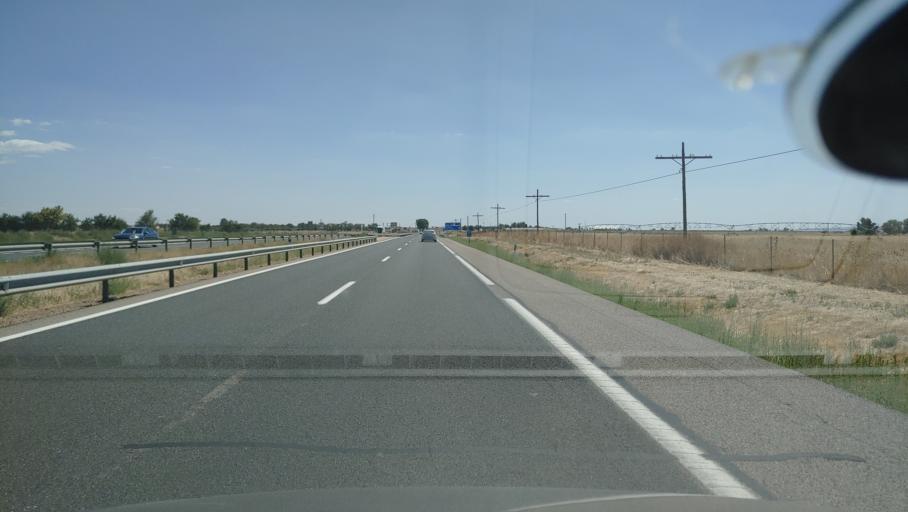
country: ES
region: Castille-La Mancha
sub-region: Provincia de Ciudad Real
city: Villarta de San Juan
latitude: 39.1326
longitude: -3.3803
